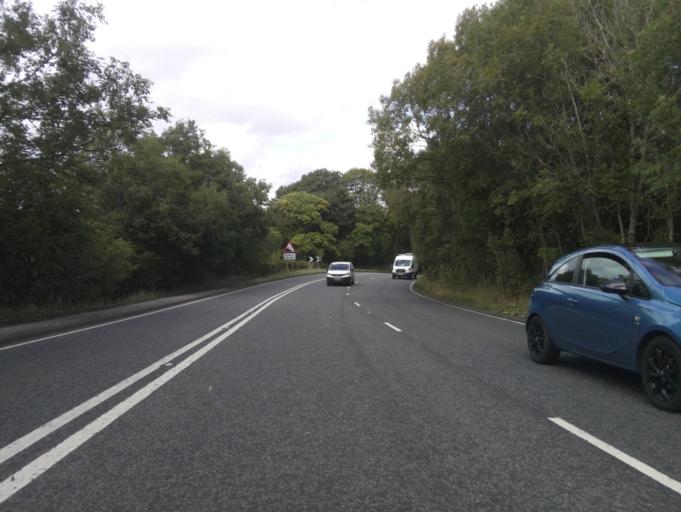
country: GB
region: England
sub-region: County Durham
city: Castleside
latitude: 54.8433
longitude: -1.8824
